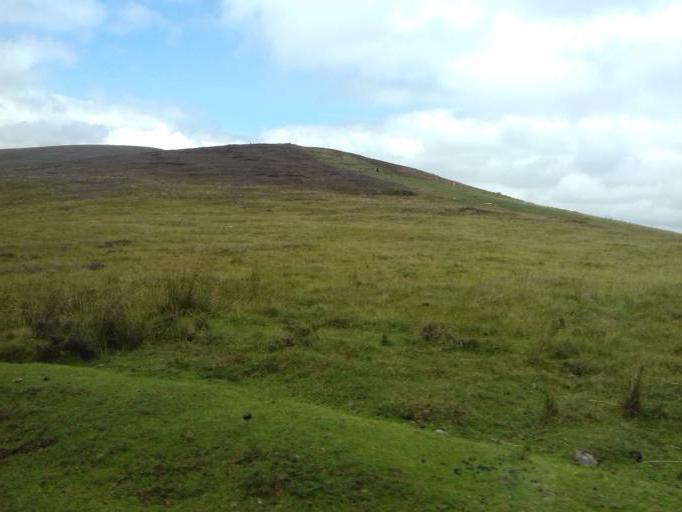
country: IE
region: Leinster
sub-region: Loch Garman
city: Bunclody
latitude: 52.6366
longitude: -6.7945
